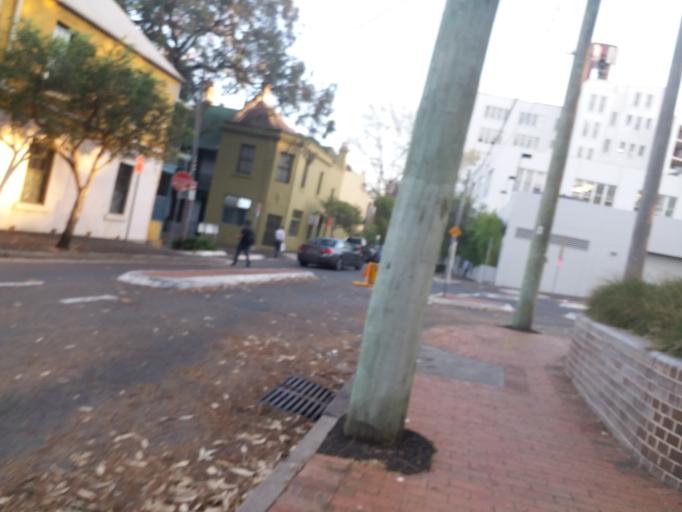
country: AU
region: New South Wales
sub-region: City of Sydney
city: Redfern
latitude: -33.8891
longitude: 151.2119
